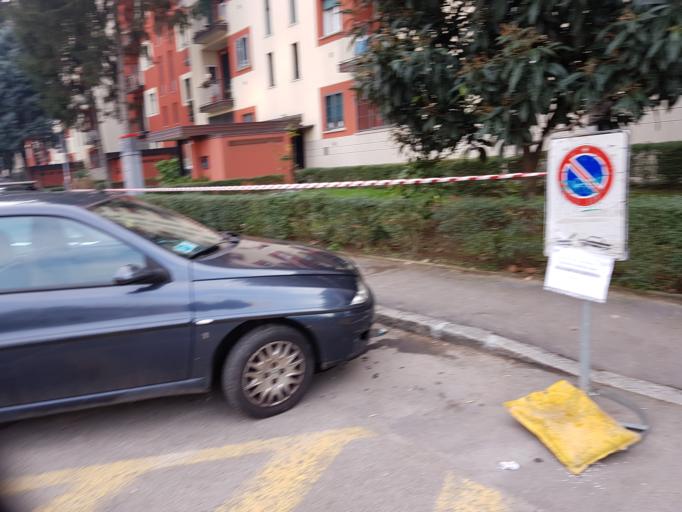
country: IT
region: Emilia-Romagna
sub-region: Provincia di Bologna
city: Quarto Inferiore
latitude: 44.5108
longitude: 11.3935
